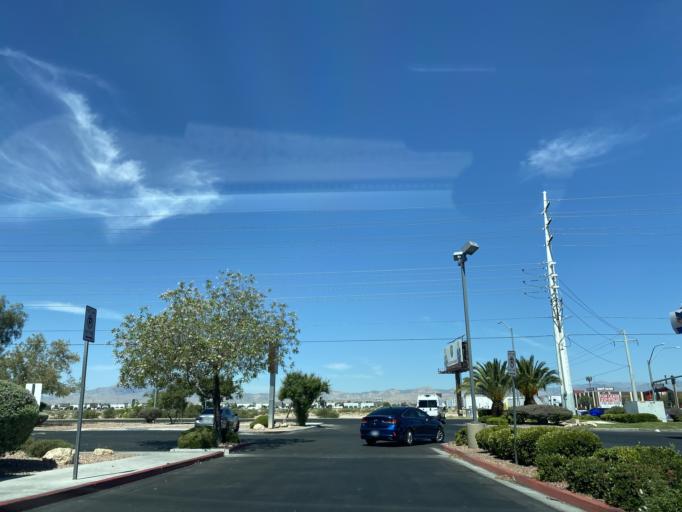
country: US
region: Nevada
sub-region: Clark County
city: Paradise
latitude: 36.0562
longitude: -115.1714
